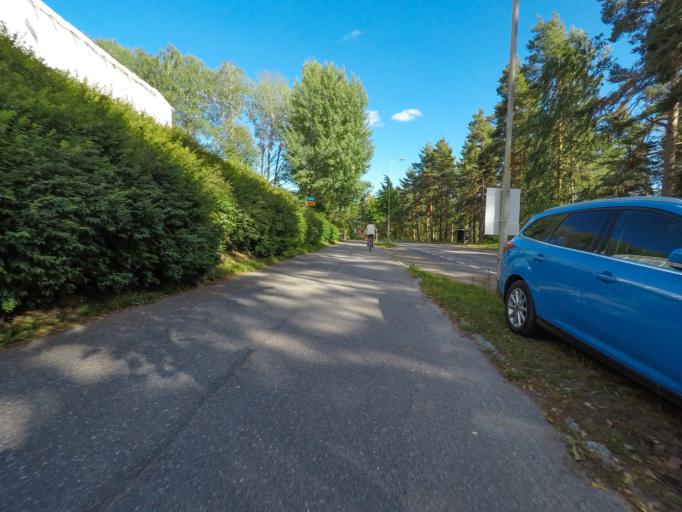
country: FI
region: South Karelia
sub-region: Lappeenranta
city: Lappeenranta
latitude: 61.0658
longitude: 28.1594
